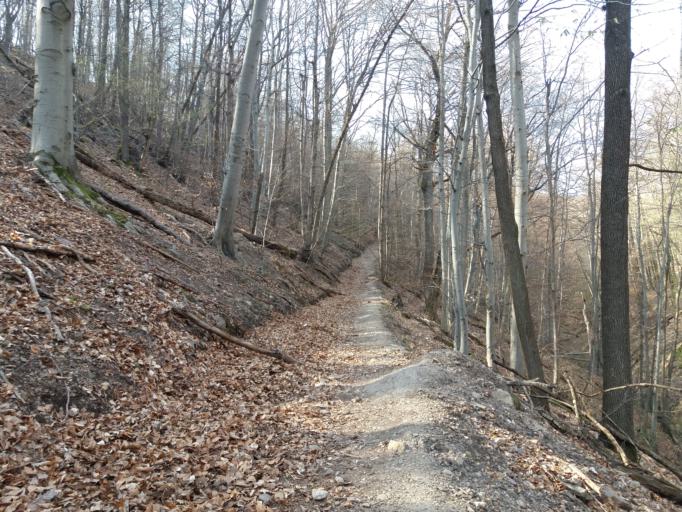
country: HU
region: Pest
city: Csobanka
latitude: 47.6768
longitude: 18.9738
